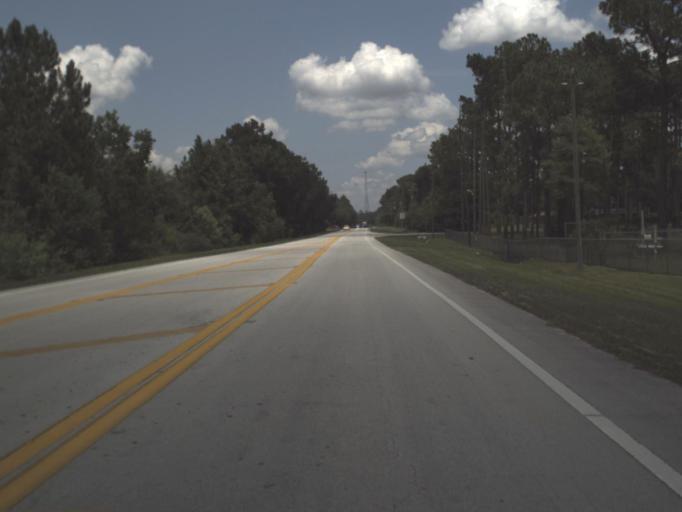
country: US
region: Florida
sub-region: Baker County
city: Macclenny
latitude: 30.2402
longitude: -82.1352
